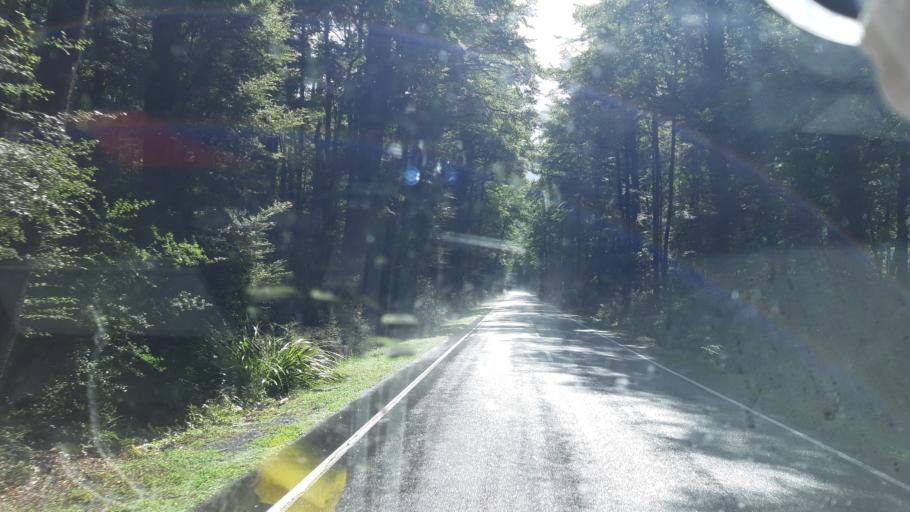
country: NZ
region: Canterbury
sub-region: Hurunui District
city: Amberley
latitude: -42.3764
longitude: 172.2737
